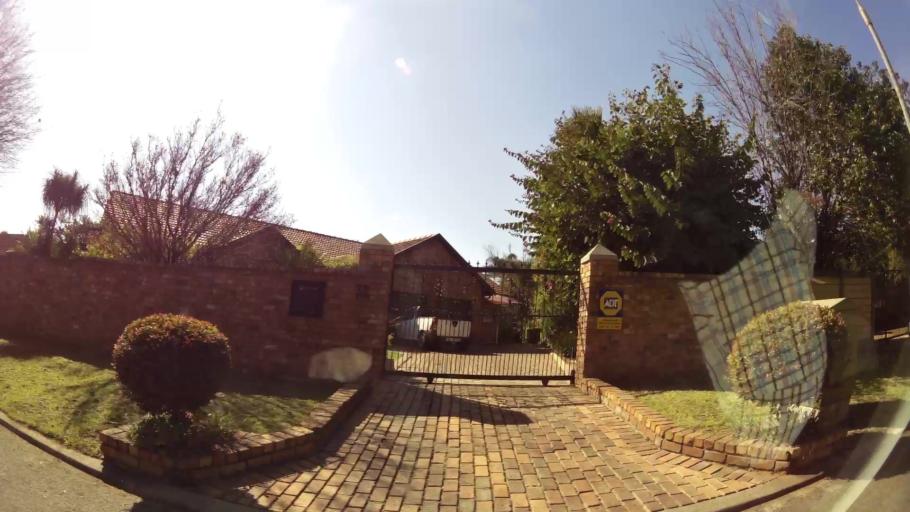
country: ZA
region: Gauteng
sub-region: Ekurhuleni Metropolitan Municipality
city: Tembisa
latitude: -26.0432
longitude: 28.2234
